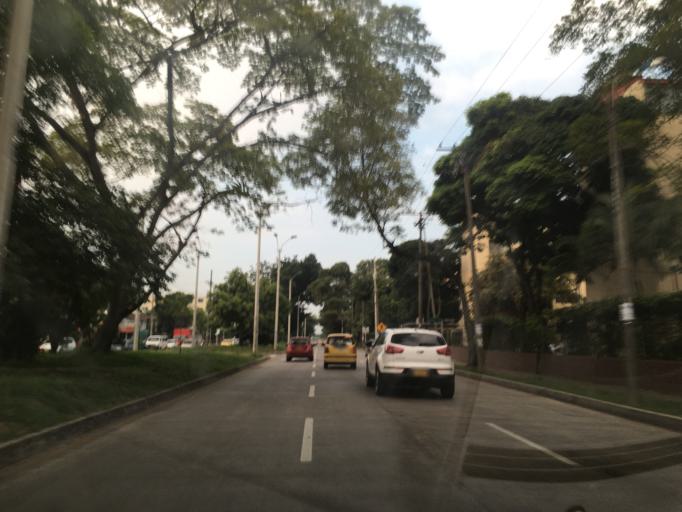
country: CO
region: Valle del Cauca
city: Cali
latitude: 3.4004
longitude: -76.5277
